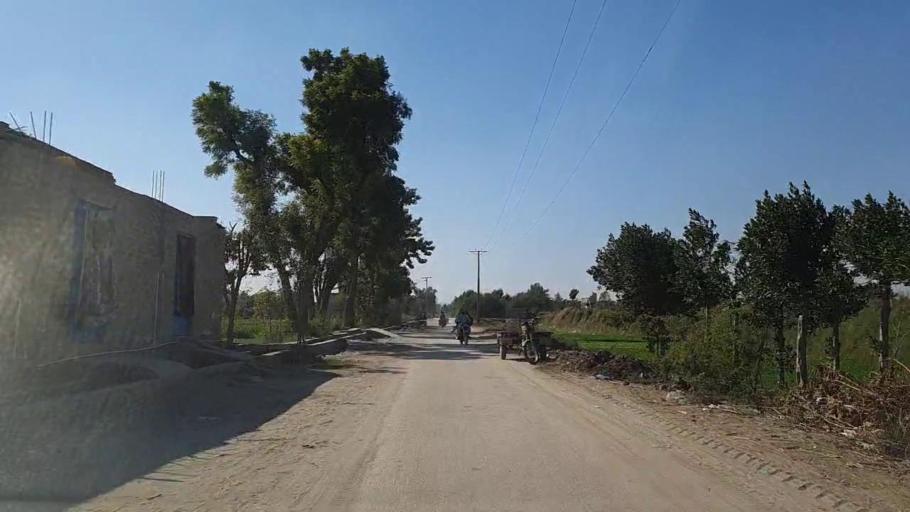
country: PK
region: Sindh
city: Nawabshah
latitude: 26.2442
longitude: 68.4292
